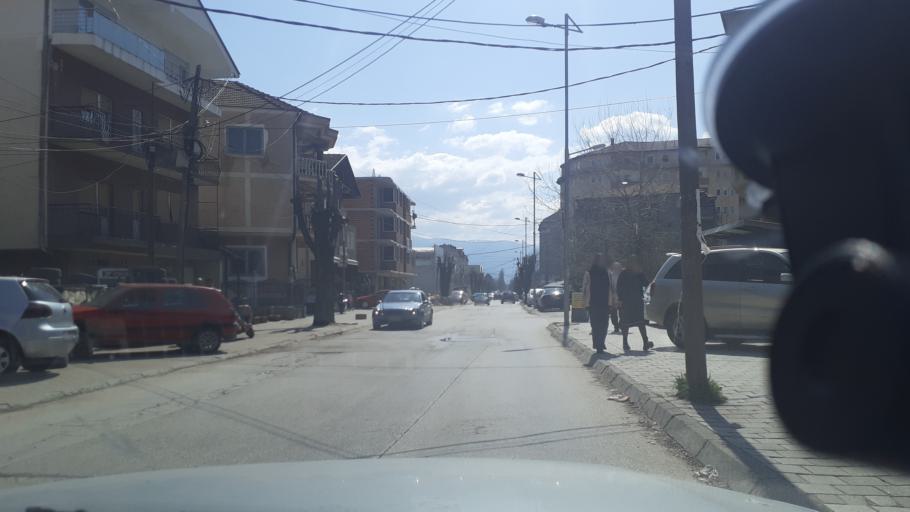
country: MK
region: Tetovo
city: Tetovo
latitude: 42.0027
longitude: 20.9693
